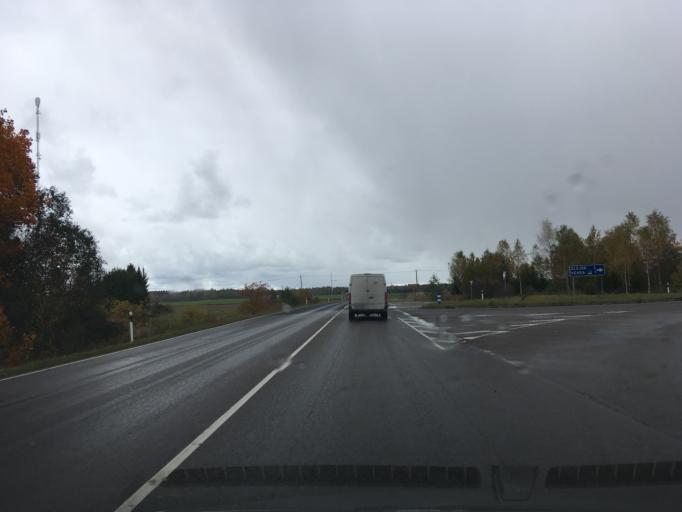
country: EE
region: Harju
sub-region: Anija vald
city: Kehra
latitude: 59.3451
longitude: 25.3134
